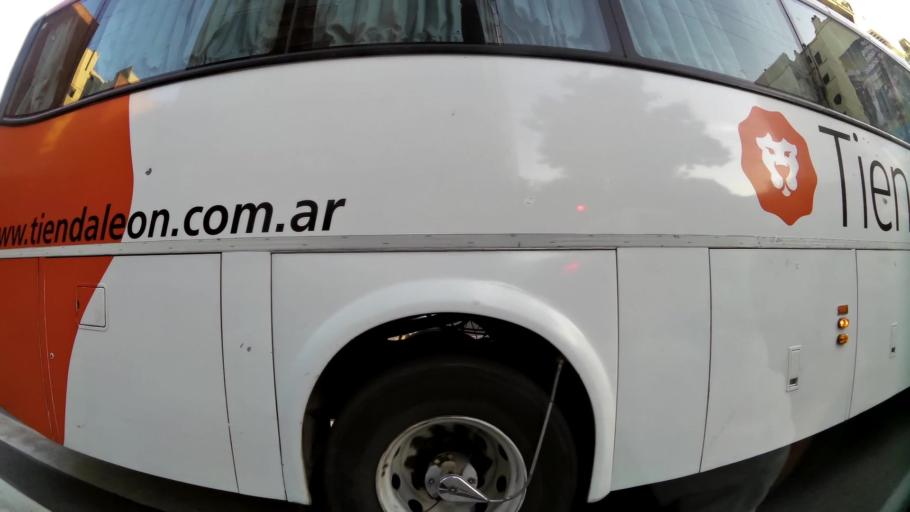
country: AR
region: Buenos Aires F.D.
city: Colegiales
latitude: -34.5915
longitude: -58.4258
